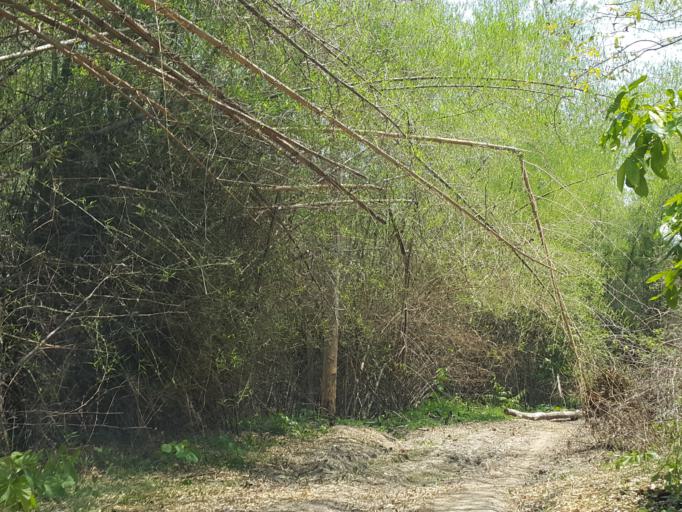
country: TH
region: Kanchanaburi
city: Sai Yok
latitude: 14.2262
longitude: 98.8813
